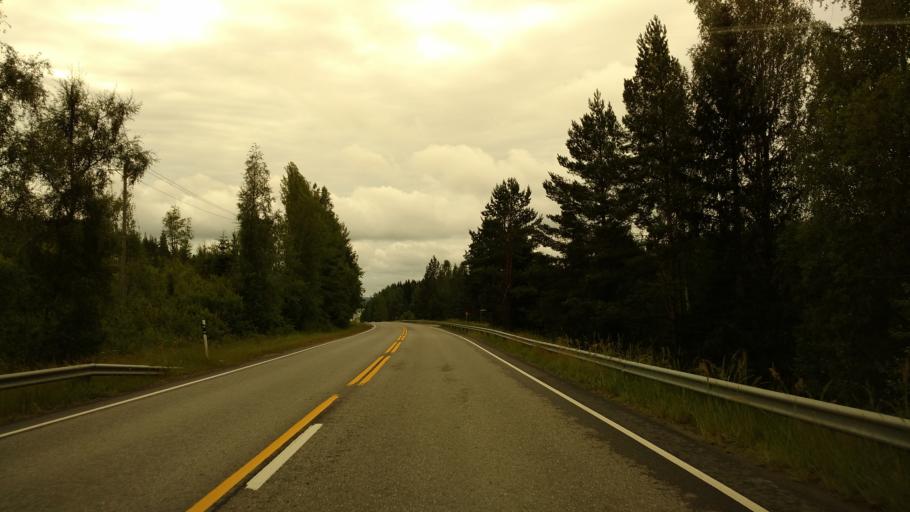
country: FI
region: Varsinais-Suomi
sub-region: Salo
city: Salo
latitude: 60.4319
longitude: 23.1743
